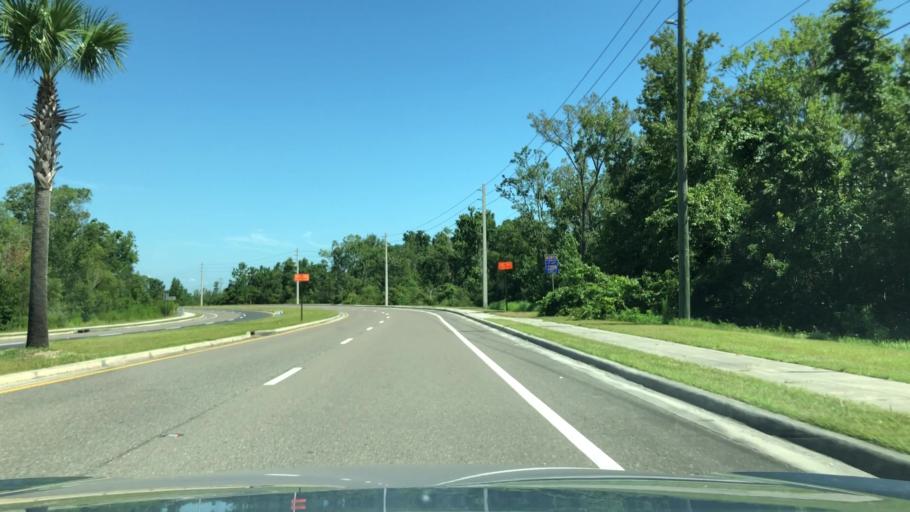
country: US
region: Florida
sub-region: Saint Johns County
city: Fruit Cove
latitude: 30.0857
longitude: -81.5322
